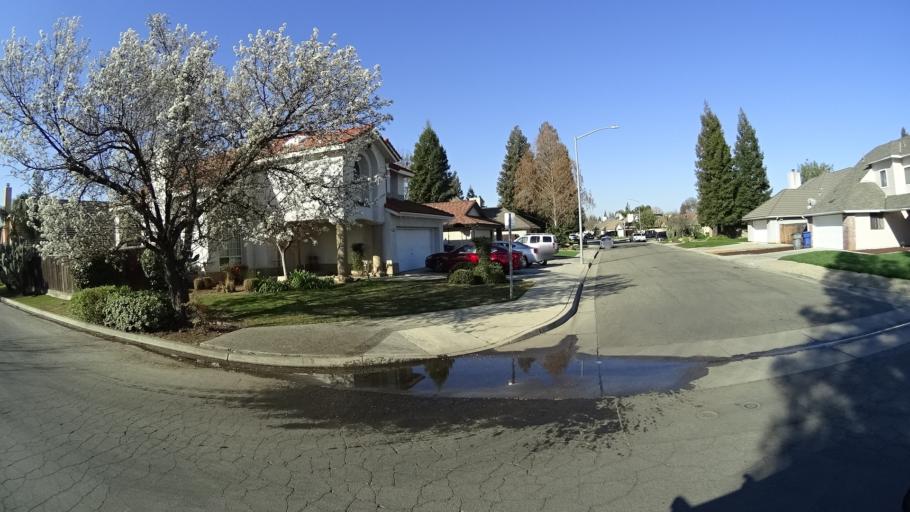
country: US
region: California
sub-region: Fresno County
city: Clovis
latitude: 36.8699
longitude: -119.7432
